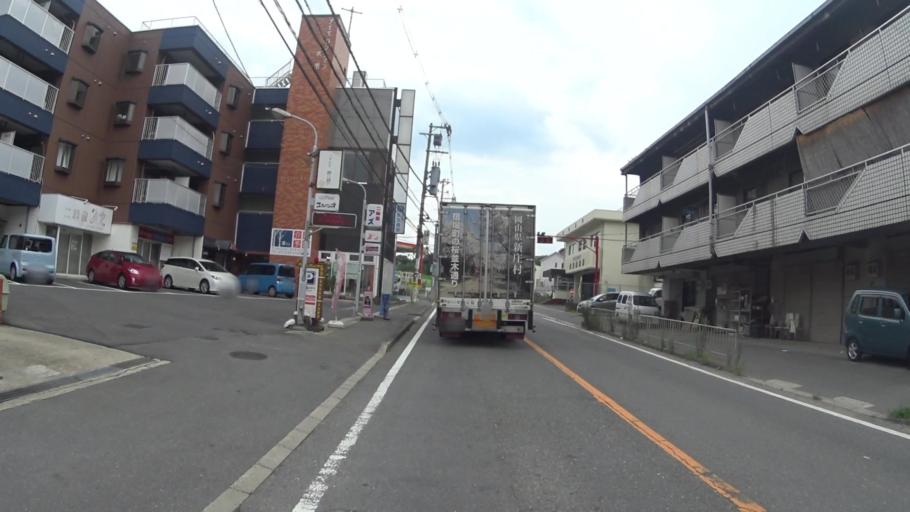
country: JP
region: Kyoto
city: Tanabe
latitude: 34.8008
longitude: 135.7341
